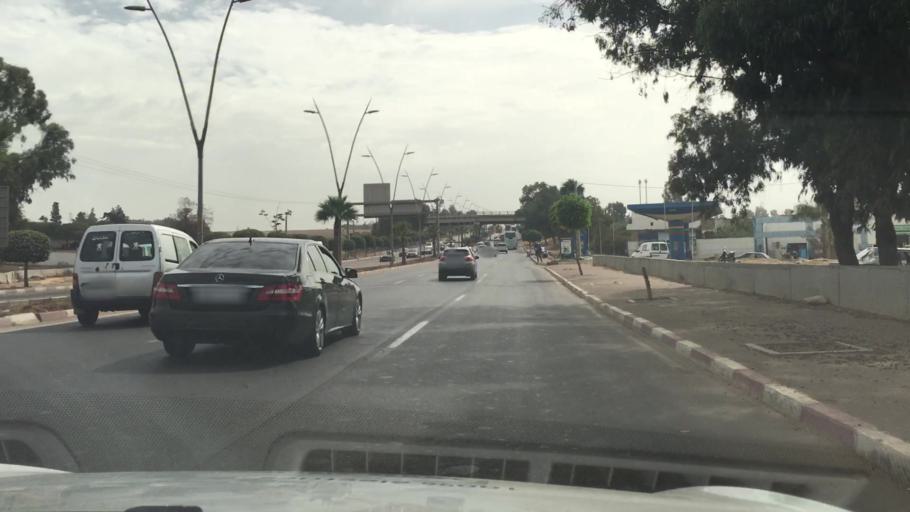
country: MA
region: Grand Casablanca
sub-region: Nouaceur
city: Bouskoura
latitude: 33.5143
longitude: -7.6313
